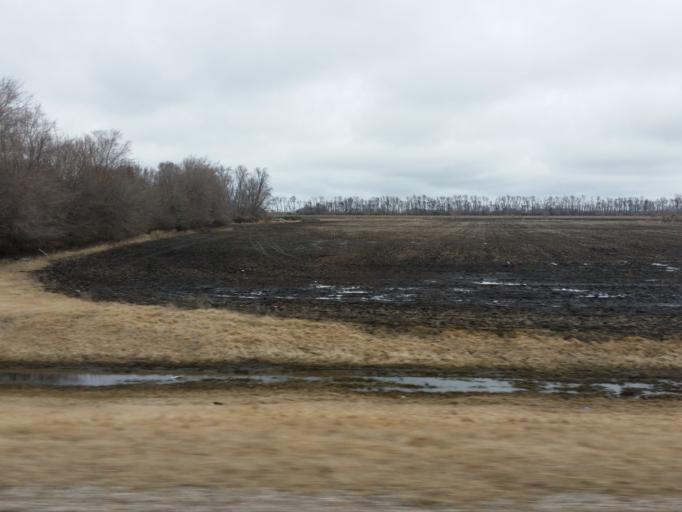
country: US
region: North Dakota
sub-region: Traill County
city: Mayville
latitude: 47.4981
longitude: -97.2926
